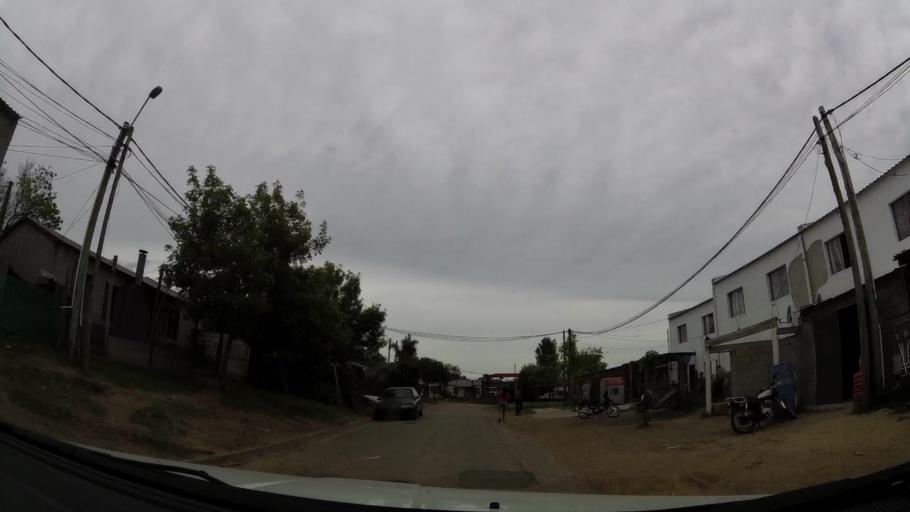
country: UY
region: Maldonado
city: Maldonado
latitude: -34.8782
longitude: -54.9773
